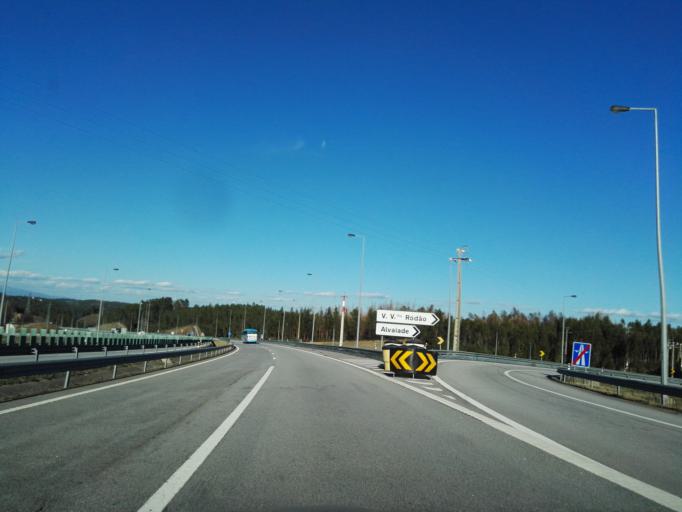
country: PT
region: Portalegre
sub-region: Nisa
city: Nisa
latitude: 39.6954
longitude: -7.6979
